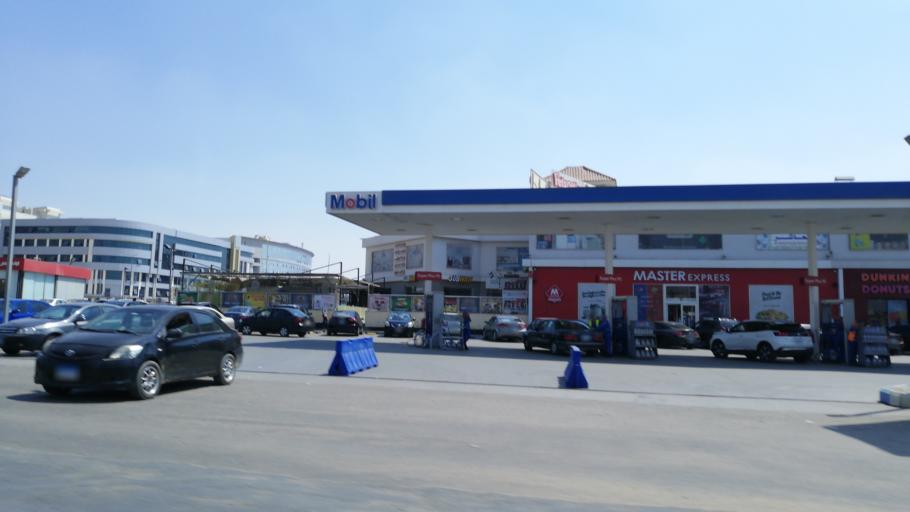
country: EG
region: Muhafazat al Qahirah
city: Cairo
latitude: 30.0212
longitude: 31.4319
